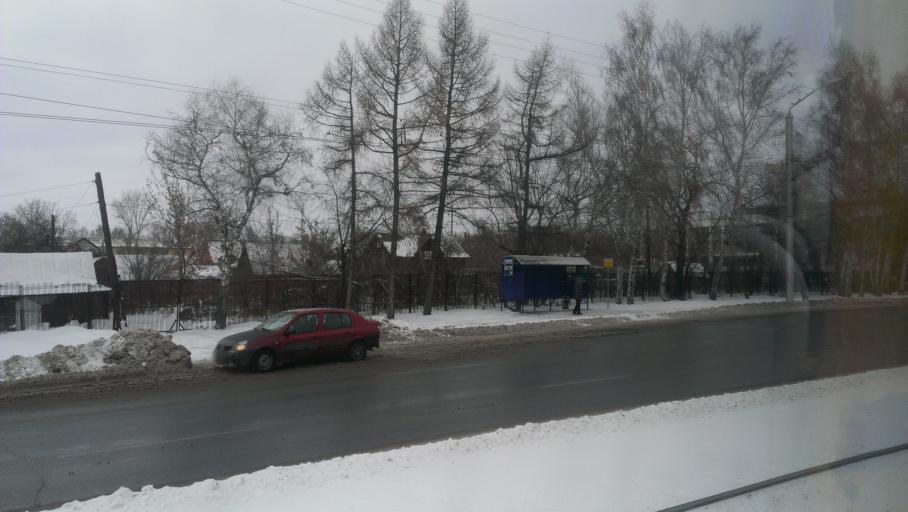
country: RU
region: Altai Krai
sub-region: Gorod Barnaulskiy
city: Barnaul
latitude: 53.3817
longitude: 83.7131
